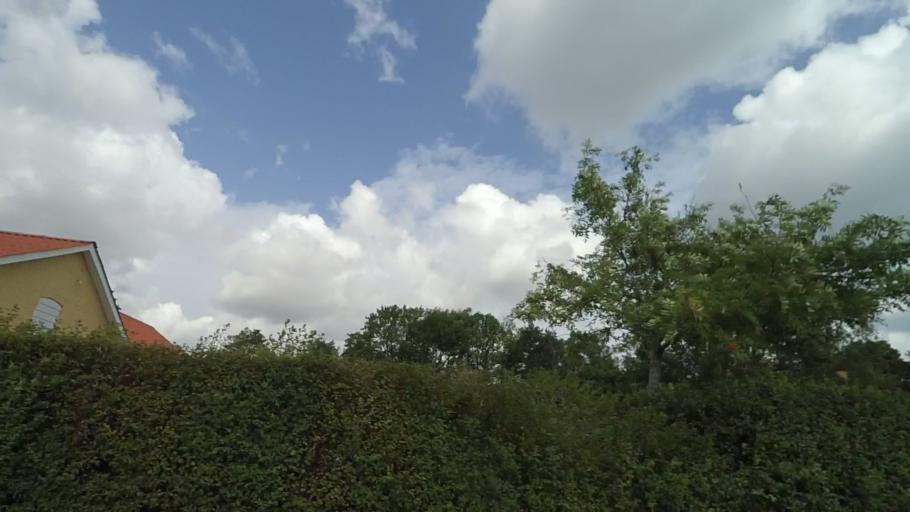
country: DK
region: Central Jutland
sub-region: Norddjurs Kommune
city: Allingabro
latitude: 56.5155
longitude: 10.3906
